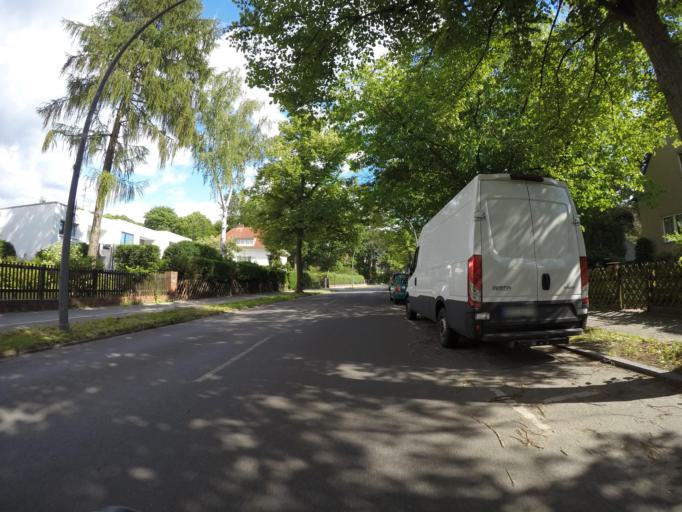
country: DE
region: Berlin
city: Dahlem
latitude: 52.4440
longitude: 13.2697
